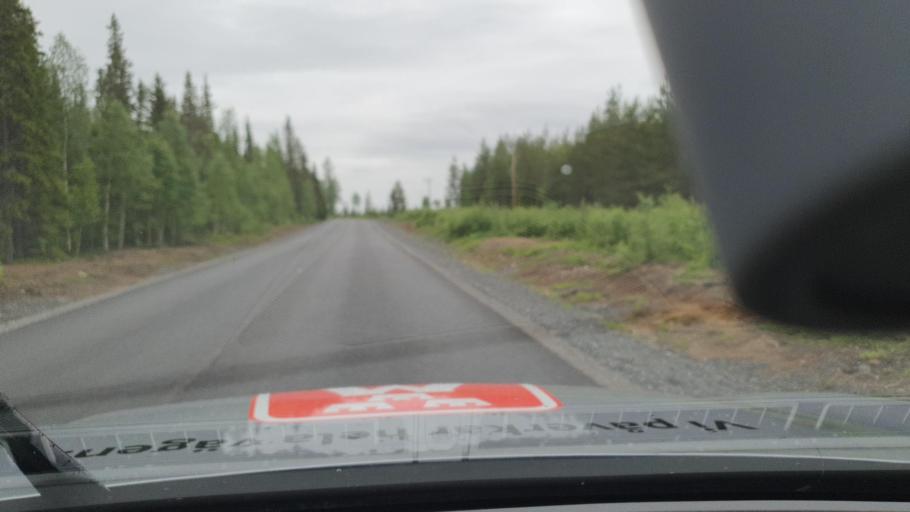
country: SE
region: Norrbotten
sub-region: Overkalix Kommun
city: OEverkalix
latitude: 66.7068
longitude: 23.2072
